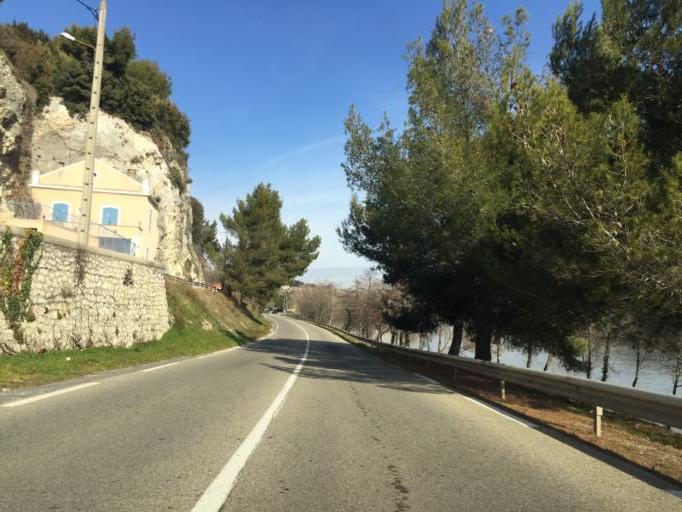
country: FR
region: Languedoc-Roussillon
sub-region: Departement du Gard
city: Villeneuve-les-Avignon
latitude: 43.9507
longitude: 4.7897
